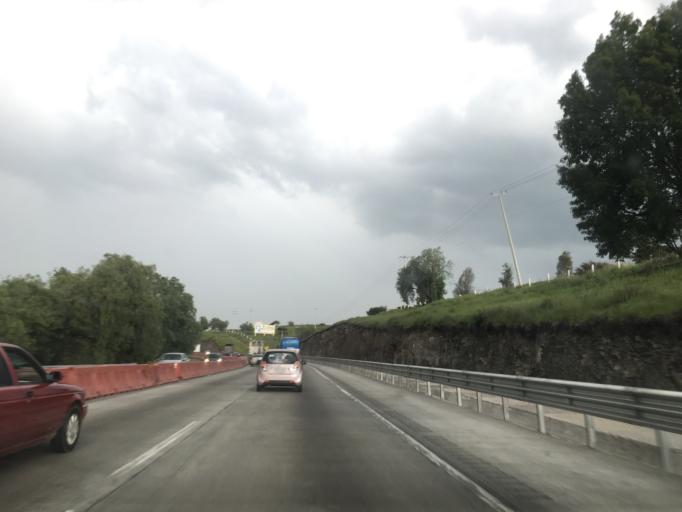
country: MX
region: Hidalgo
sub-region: Tepeji del Rio de Ocampo
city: Cantera de Villagran
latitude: 19.8624
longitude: -99.3204
